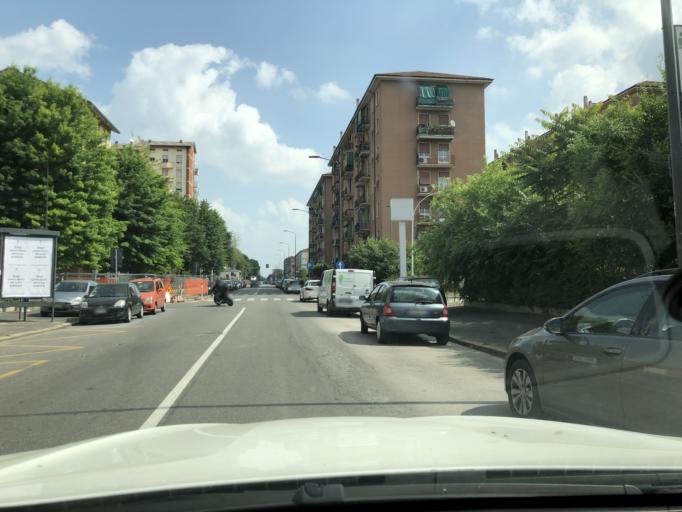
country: IT
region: Lombardy
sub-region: Citta metropolitana di Milano
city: Bresso
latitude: 45.5103
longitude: 9.1999
